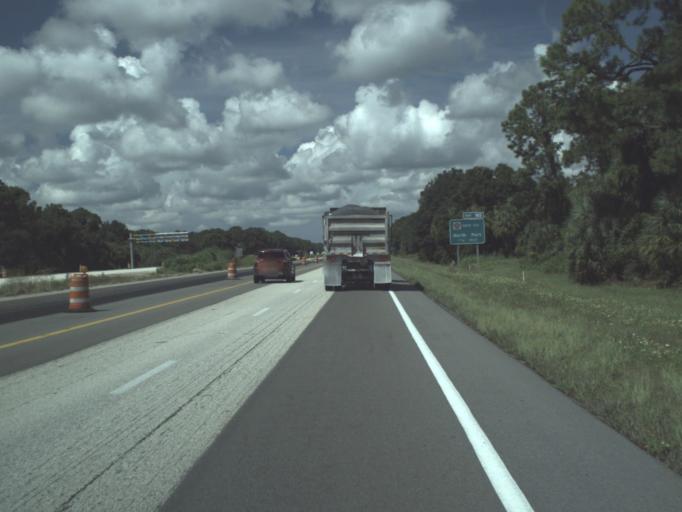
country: US
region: Florida
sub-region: Sarasota County
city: North Port
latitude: 27.0993
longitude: -82.1766
